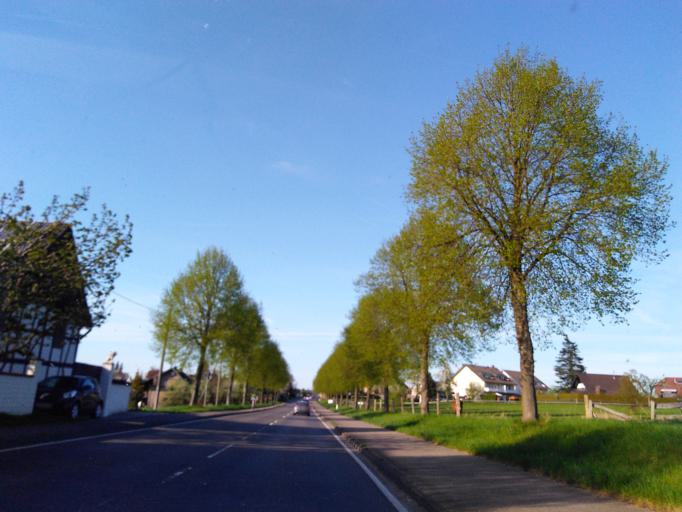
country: DE
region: North Rhine-Westphalia
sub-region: Regierungsbezirk Koln
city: Hennef
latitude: 50.8294
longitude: 7.2817
